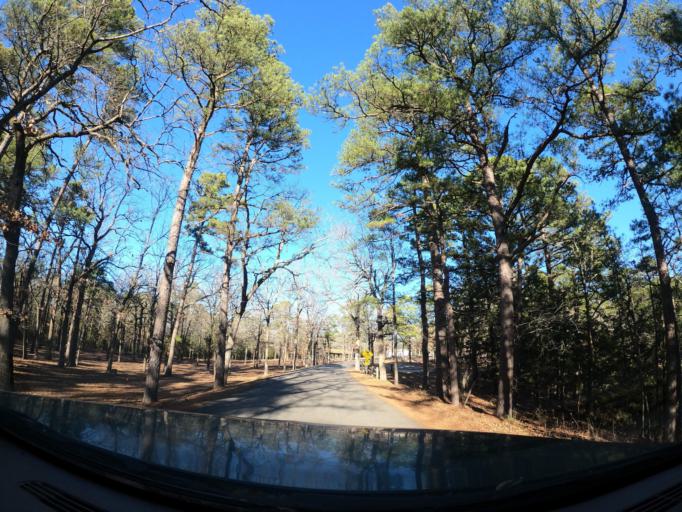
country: US
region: Oklahoma
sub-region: Latimer County
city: Wilburton
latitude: 34.9813
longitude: -95.3561
